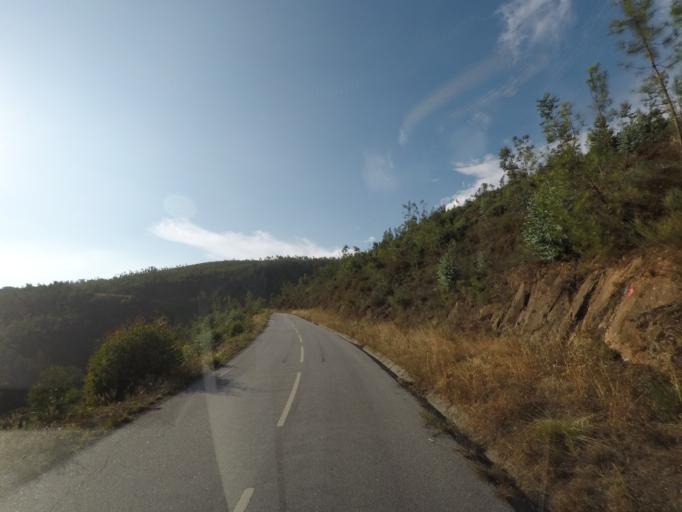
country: PT
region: Vila Real
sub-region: Mesao Frio
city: Mesao Frio
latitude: 41.1635
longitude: -7.9072
